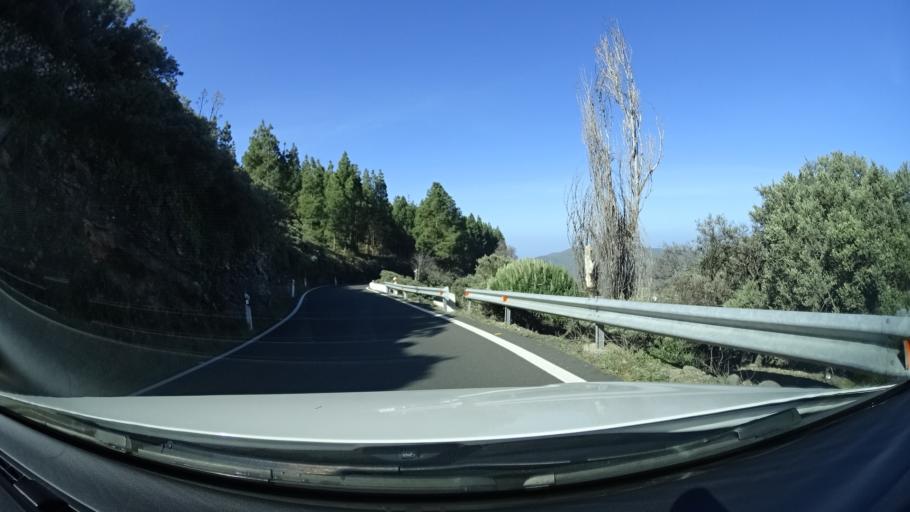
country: ES
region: Canary Islands
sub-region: Provincia de Las Palmas
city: Artenara
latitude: 28.0269
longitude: -15.6215
